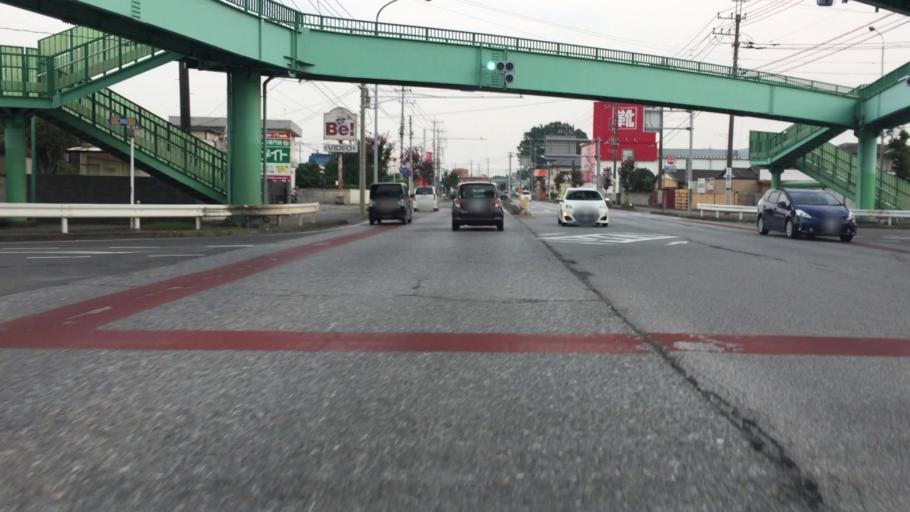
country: JP
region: Tochigi
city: Tochigi
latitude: 36.3742
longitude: 139.7155
